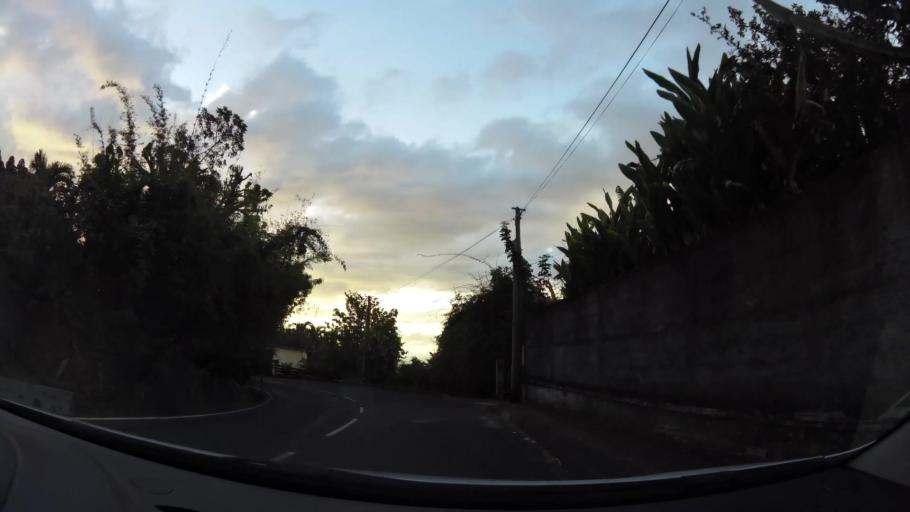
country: RE
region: Reunion
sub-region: Reunion
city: Saint-Denis
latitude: -20.9172
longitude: 55.4599
